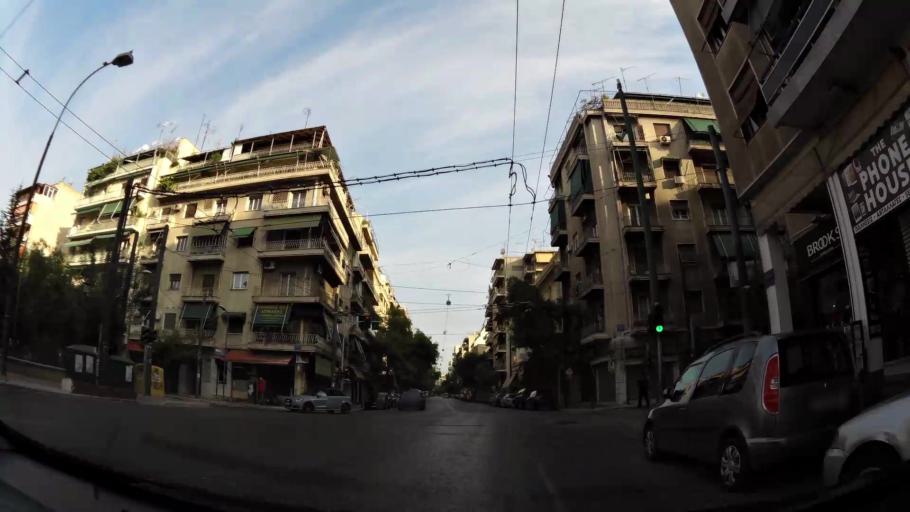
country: GR
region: Attica
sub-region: Nomarchia Athinas
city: Kipseli
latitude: 37.9973
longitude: 23.7275
